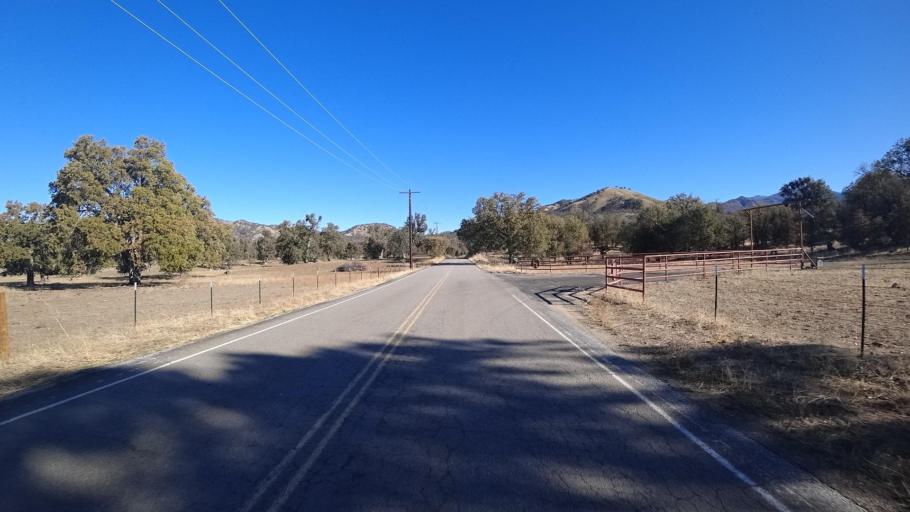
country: US
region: California
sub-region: Kern County
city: Alta Sierra
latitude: 35.7760
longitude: -118.7052
